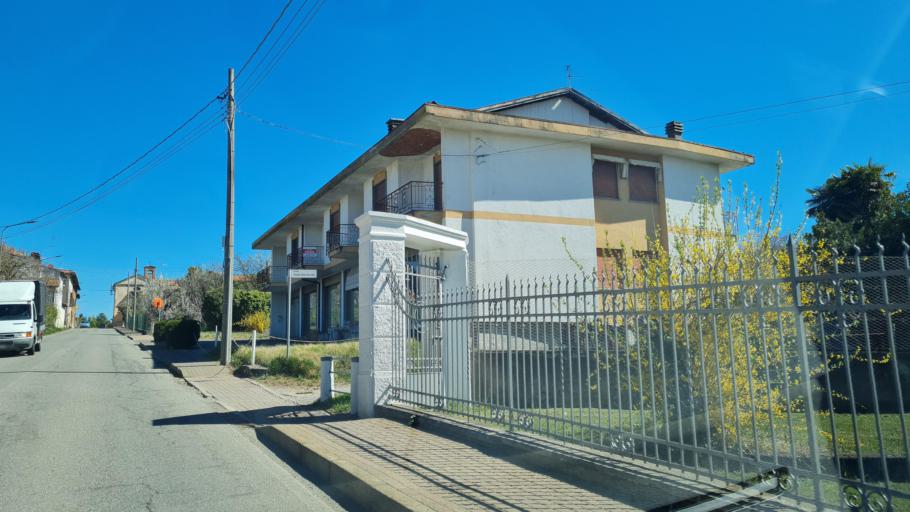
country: IT
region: Piedmont
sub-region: Provincia di Novara
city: Boca
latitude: 45.6840
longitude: 8.4120
